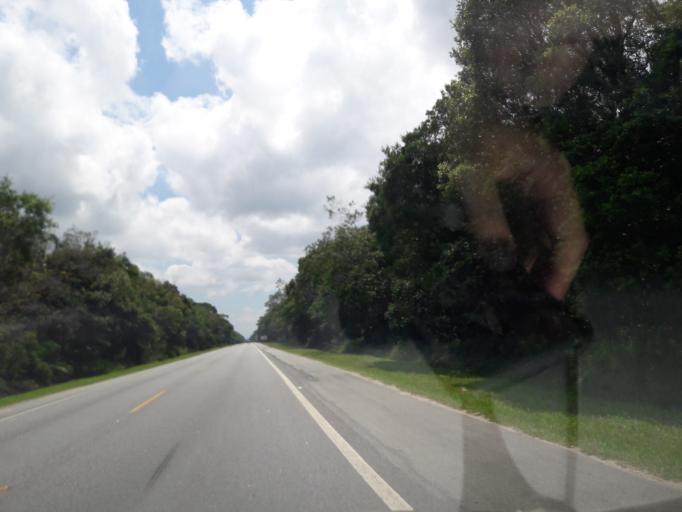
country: BR
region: Parana
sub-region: Pontal Do Parana
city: Pontal do Parana
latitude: -25.6360
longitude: -48.5361
